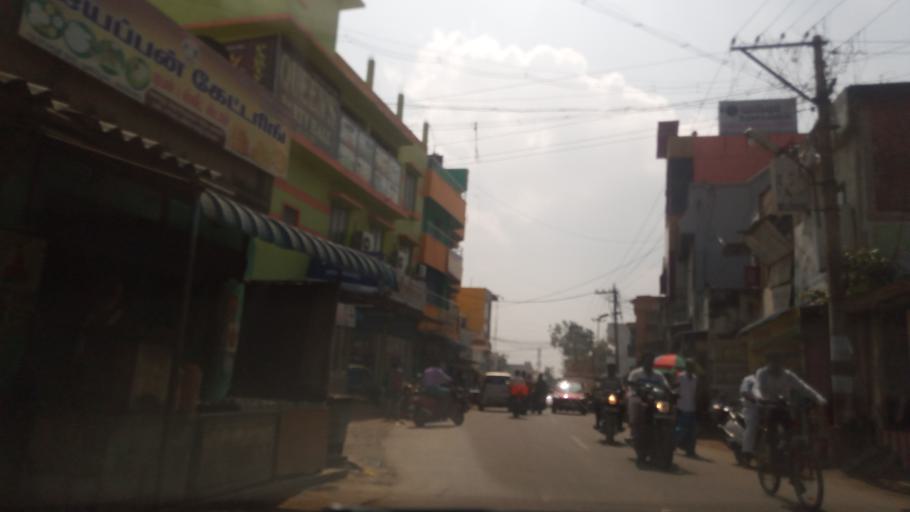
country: IN
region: Tamil Nadu
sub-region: Vellore
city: Arakkonam
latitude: 13.0811
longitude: 79.6711
